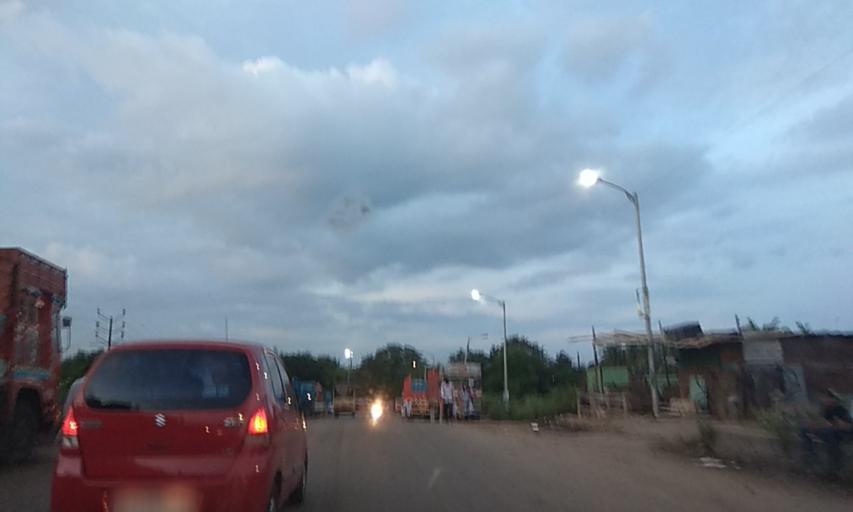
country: IN
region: Maharashtra
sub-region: Pune Division
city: Pune
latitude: 18.5186
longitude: 73.9155
